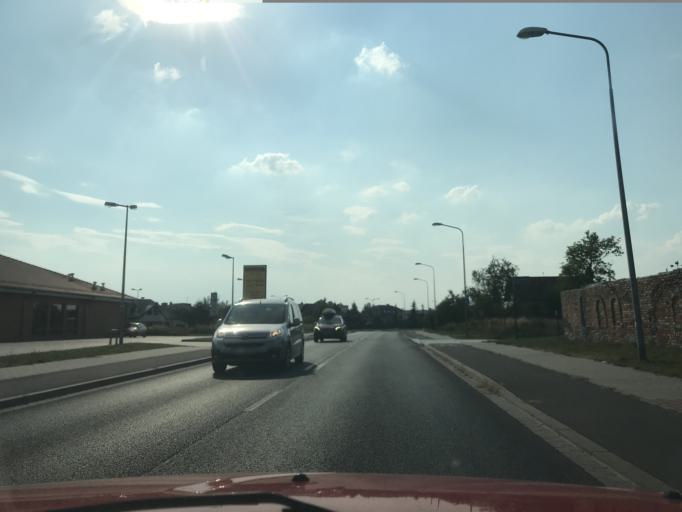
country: PL
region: Greater Poland Voivodeship
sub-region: Powiat poznanski
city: Plewiska
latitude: 52.3788
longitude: 16.8249
